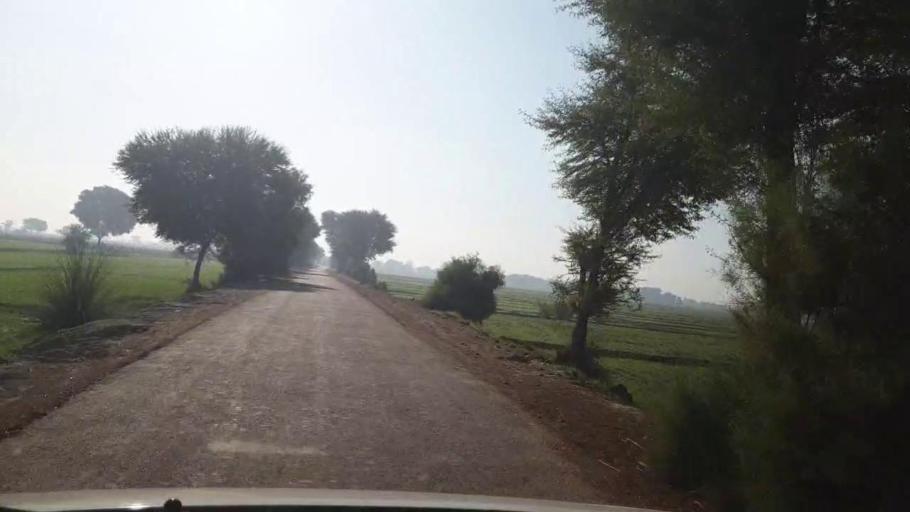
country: PK
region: Sindh
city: Dadu
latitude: 26.6627
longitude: 67.8187
